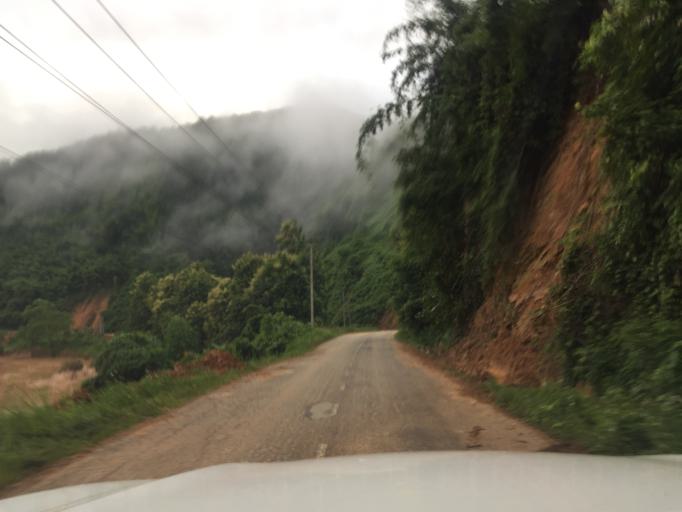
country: LA
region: Phongsali
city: Khoa
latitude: 21.0745
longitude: 102.3769
